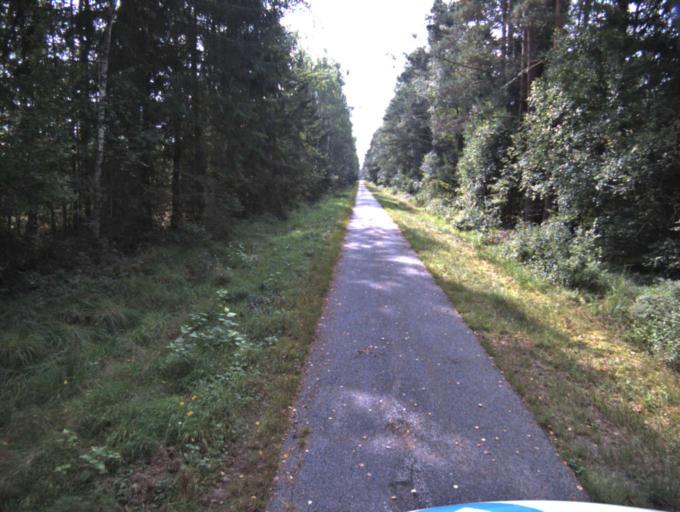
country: SE
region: Vaestra Goetaland
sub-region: Tranemo Kommun
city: Limmared
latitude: 57.6202
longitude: 13.3449
